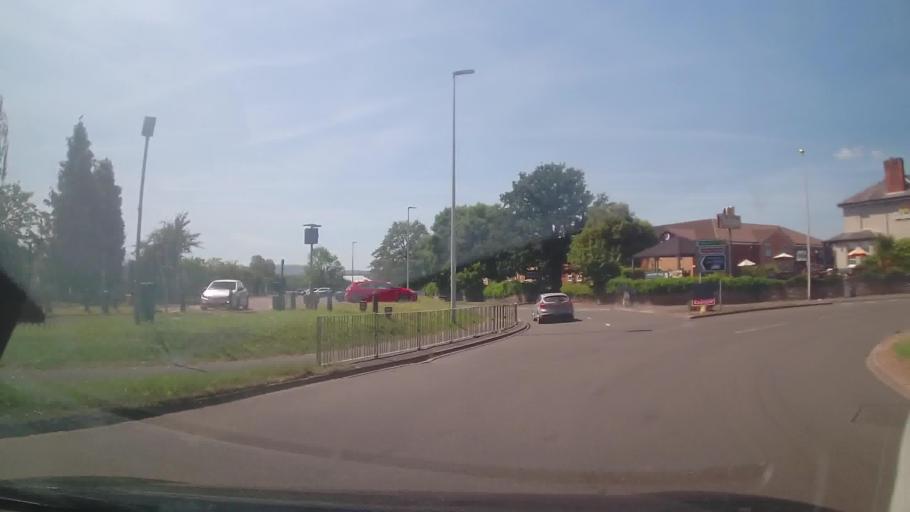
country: GB
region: England
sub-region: Herefordshire
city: Hereford
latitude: 52.0750
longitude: -2.7217
